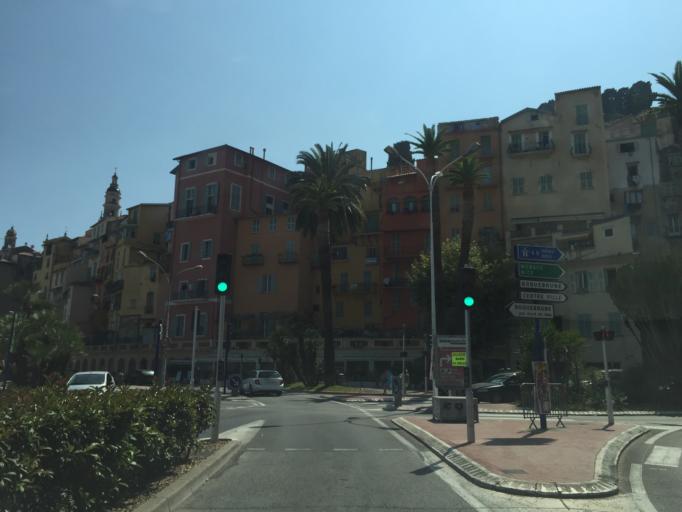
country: FR
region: Provence-Alpes-Cote d'Azur
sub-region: Departement des Alpes-Maritimes
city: Menton
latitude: 43.7791
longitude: 7.5075
